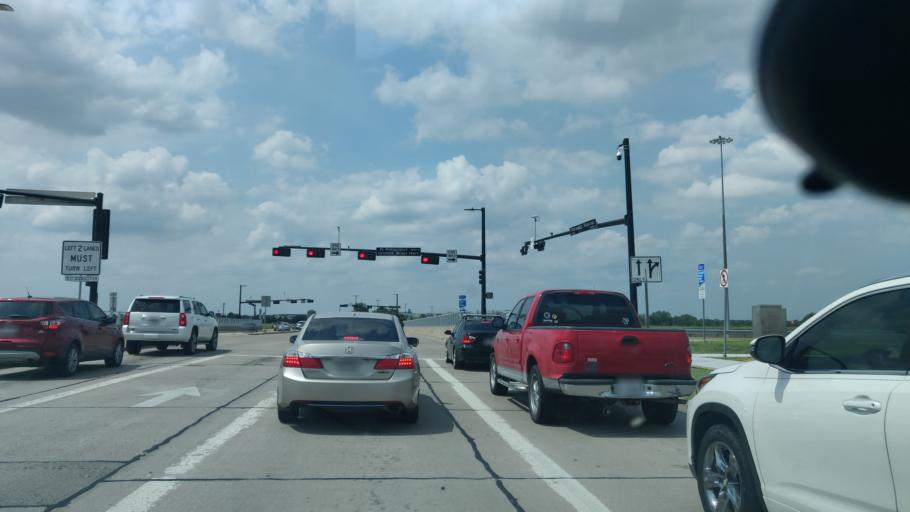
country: US
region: Texas
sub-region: Dallas County
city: Sachse
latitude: 32.9465
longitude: -96.6091
